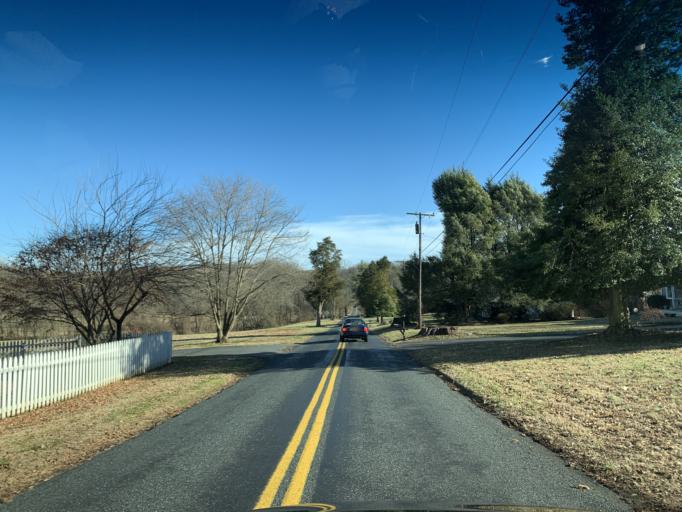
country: US
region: Maryland
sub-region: Harford County
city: Riverside
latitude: 39.5451
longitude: -76.2511
